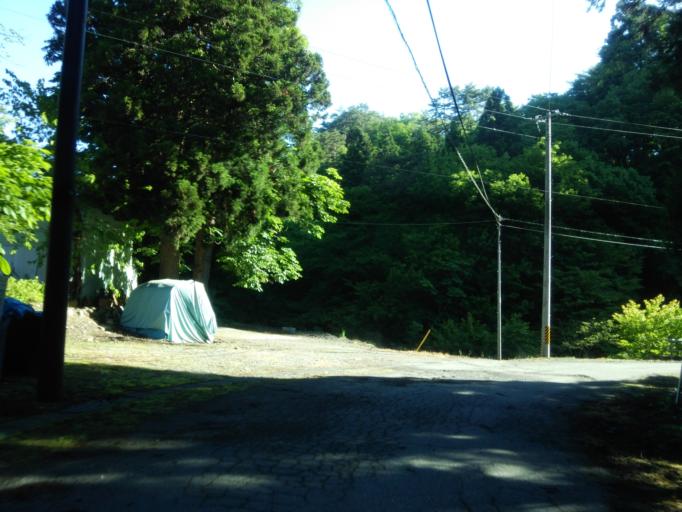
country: JP
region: Fukushima
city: Kitakata
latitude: 37.3759
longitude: 139.8056
